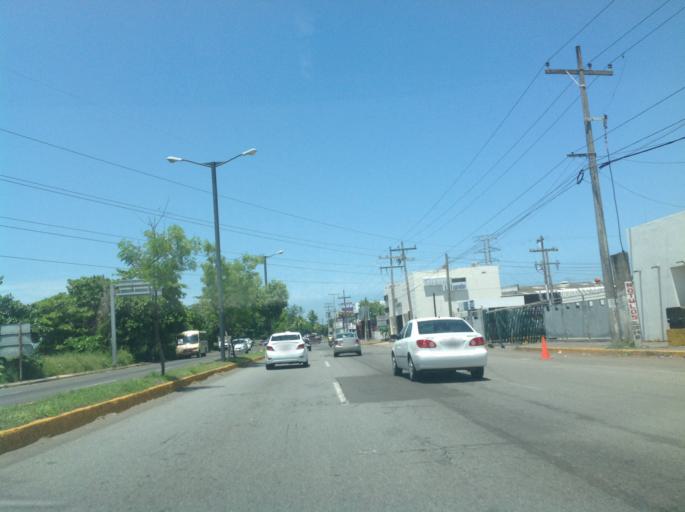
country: MX
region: Veracruz
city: Veracruz
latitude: 19.1445
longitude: -96.1459
